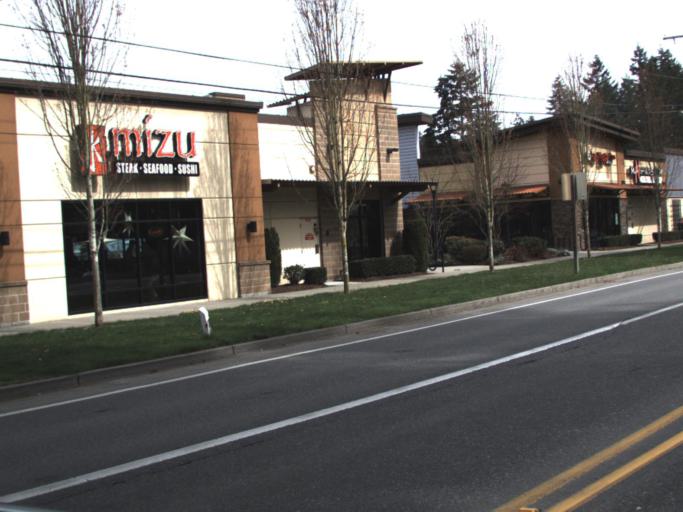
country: US
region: Washington
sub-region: King County
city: Covington
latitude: 47.3580
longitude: -122.0974
